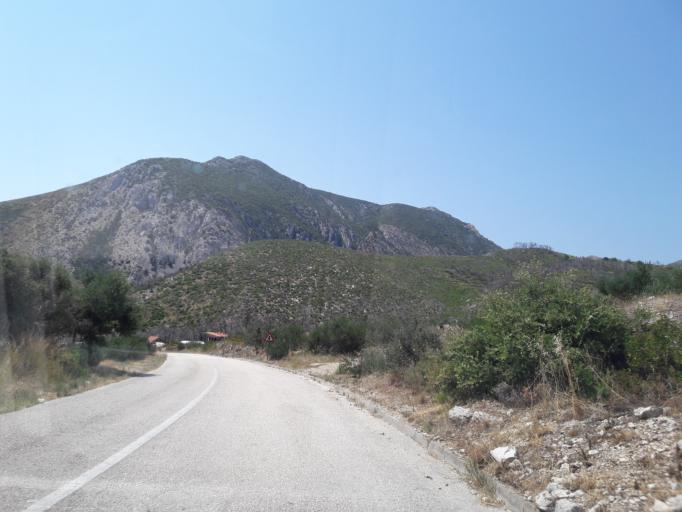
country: HR
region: Dubrovacko-Neretvanska
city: Blato
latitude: 42.9189
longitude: 17.4061
